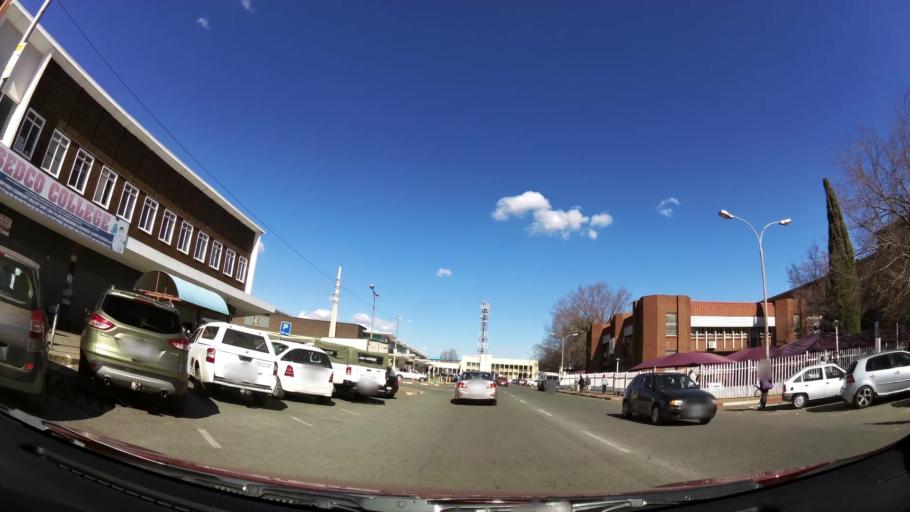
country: ZA
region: Gauteng
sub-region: West Rand District Municipality
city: Carletonville
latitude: -26.3566
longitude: 27.3975
